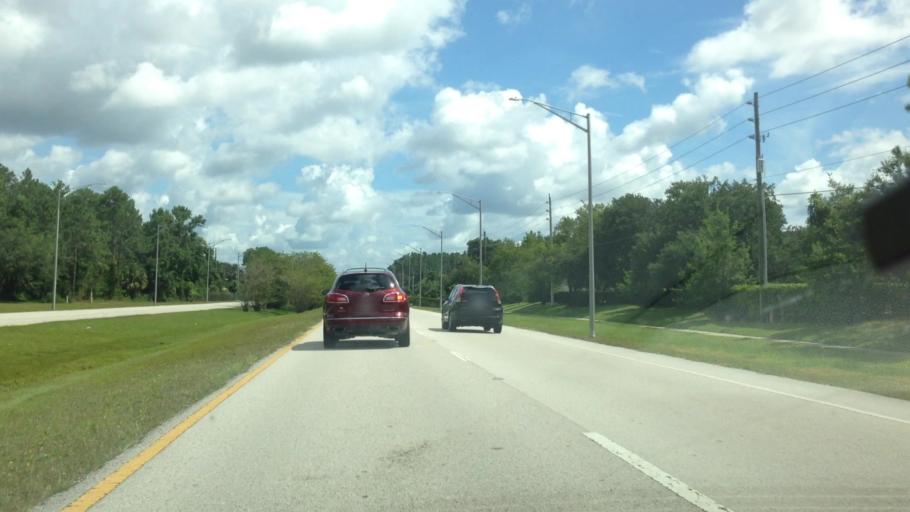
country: US
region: Florida
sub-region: Duval County
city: Jacksonville Beach
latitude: 30.2755
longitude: -81.4614
